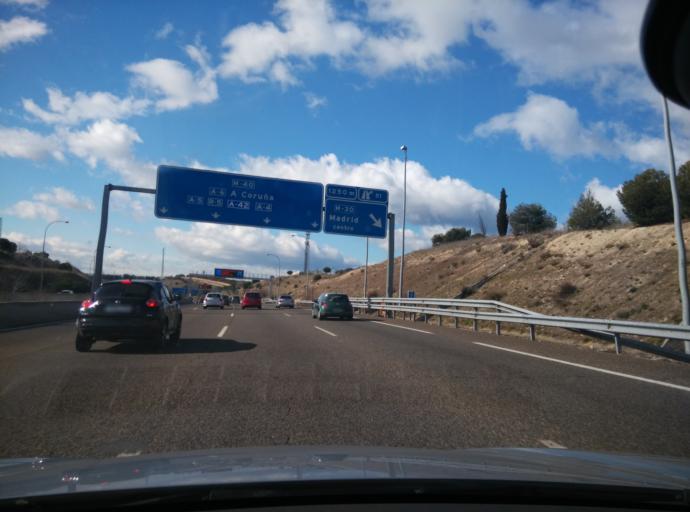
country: ES
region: Madrid
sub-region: Provincia de Madrid
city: Fuencarral-El Pardo
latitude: 40.4919
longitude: -3.7369
